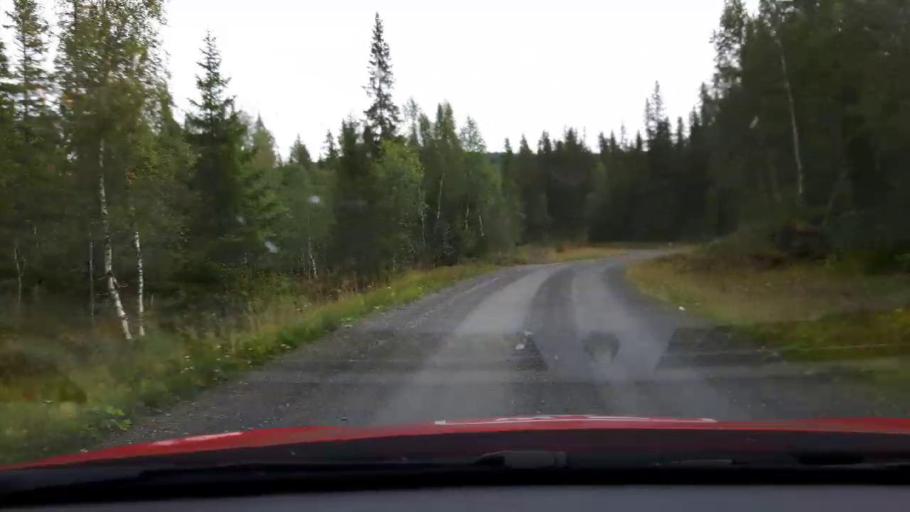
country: SE
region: Jaemtland
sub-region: Are Kommun
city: Are
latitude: 63.7733
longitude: 13.0741
